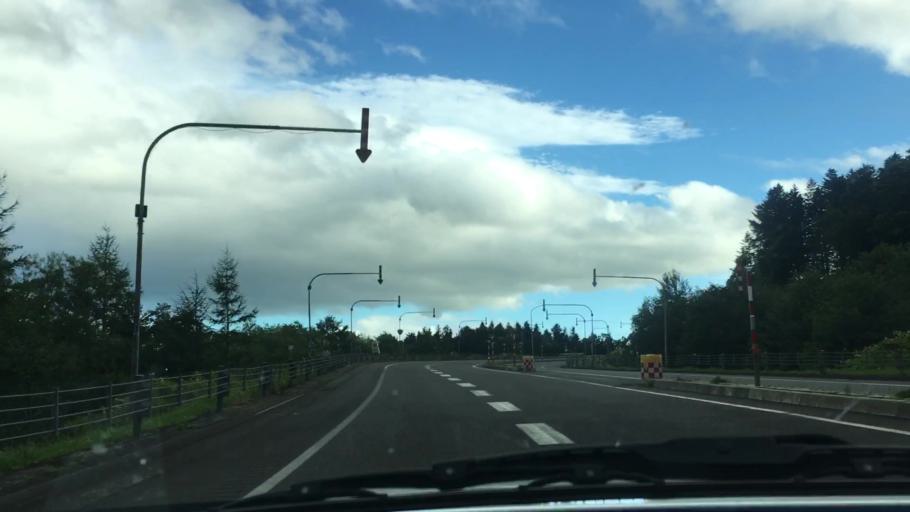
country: JP
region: Hokkaido
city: Otofuke
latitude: 43.1630
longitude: 142.8038
